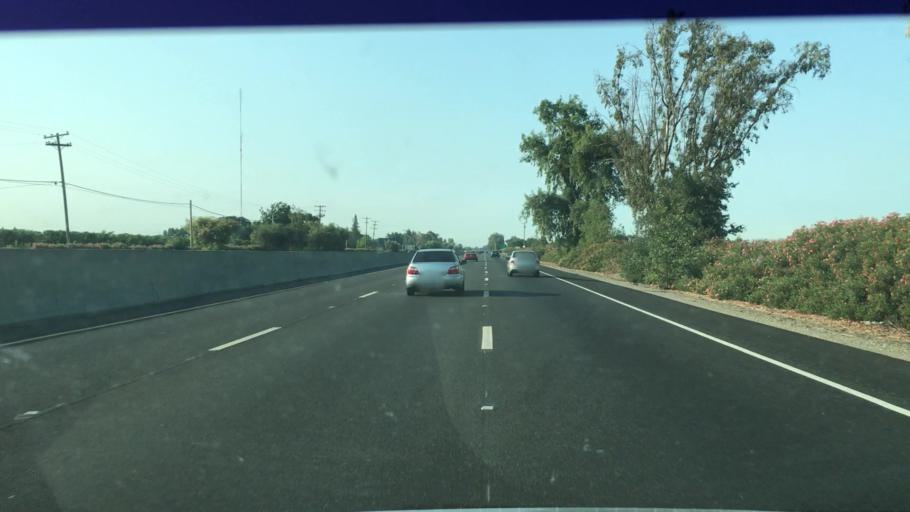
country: US
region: California
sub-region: San Joaquin County
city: Morada
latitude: 38.0764
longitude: -121.2600
